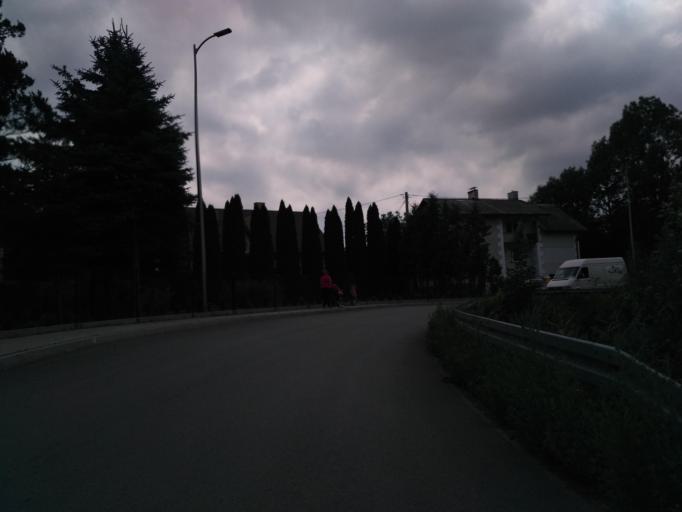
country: PL
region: Subcarpathian Voivodeship
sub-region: Powiat krosnienski
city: Iwonicz-Zdroj
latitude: 49.5741
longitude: 21.8196
